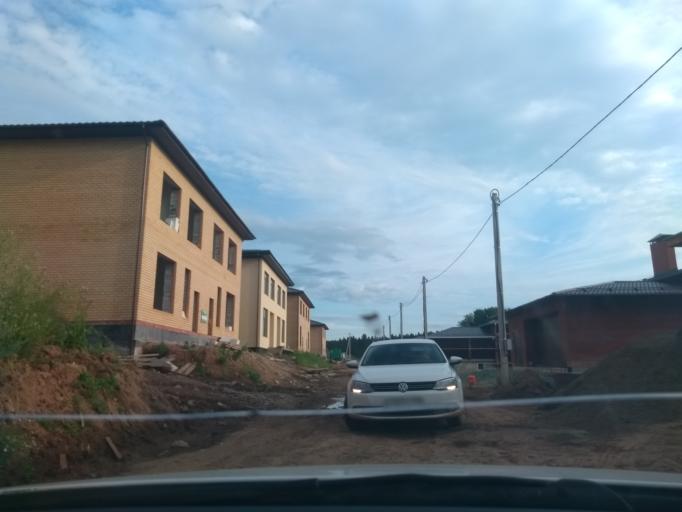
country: RU
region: Perm
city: Perm
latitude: 57.9996
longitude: 56.3217
